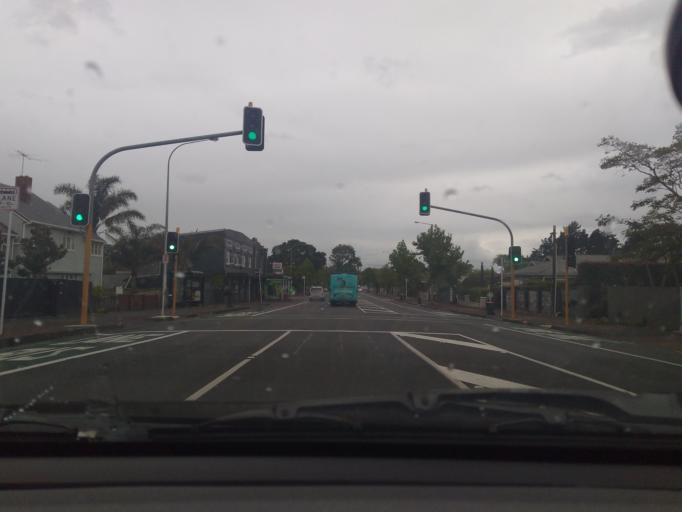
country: NZ
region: Auckland
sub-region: Auckland
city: Rosebank
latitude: -36.8684
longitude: 174.7157
